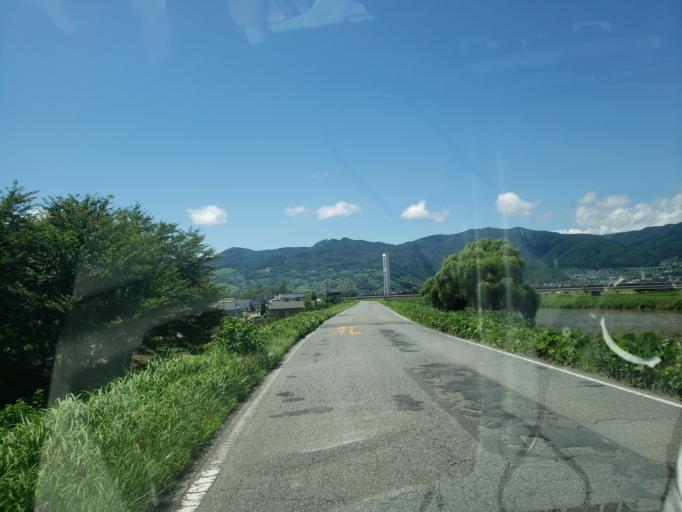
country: JP
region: Nagano
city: Nagano-shi
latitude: 36.5351
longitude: 138.1142
